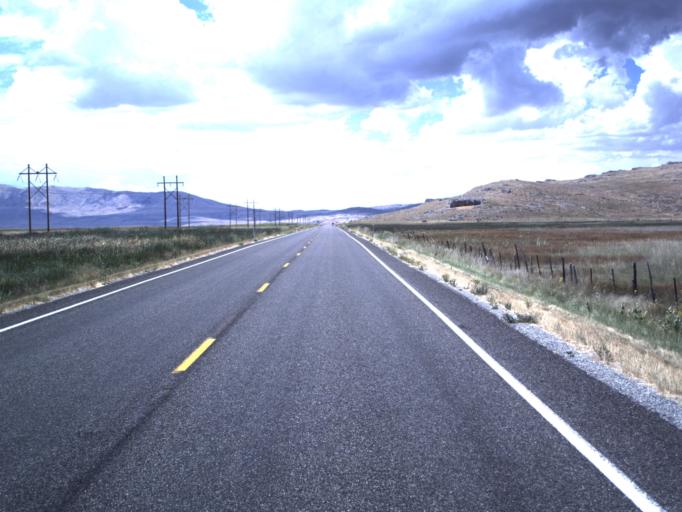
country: US
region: Utah
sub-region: Box Elder County
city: Tremonton
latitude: 41.6115
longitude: -112.3554
